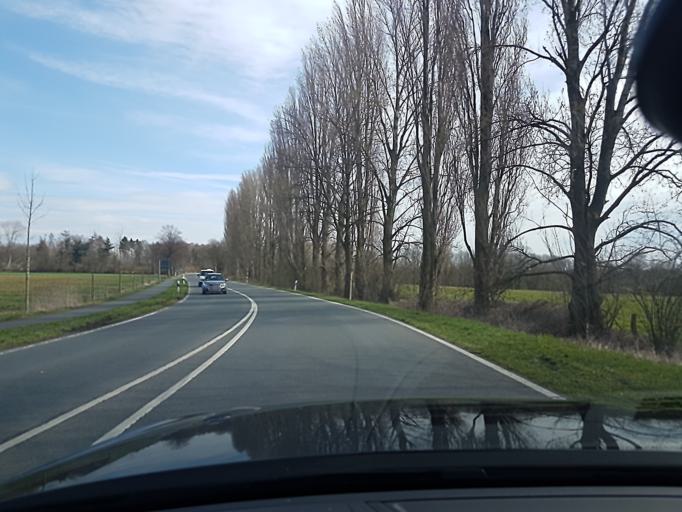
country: DE
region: North Rhine-Westphalia
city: Werne
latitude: 51.6478
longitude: 7.6051
